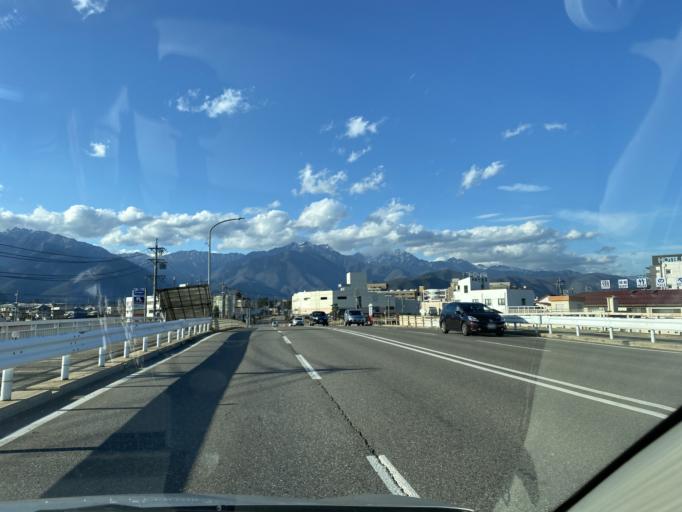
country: JP
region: Nagano
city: Omachi
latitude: 36.4979
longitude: 137.8603
